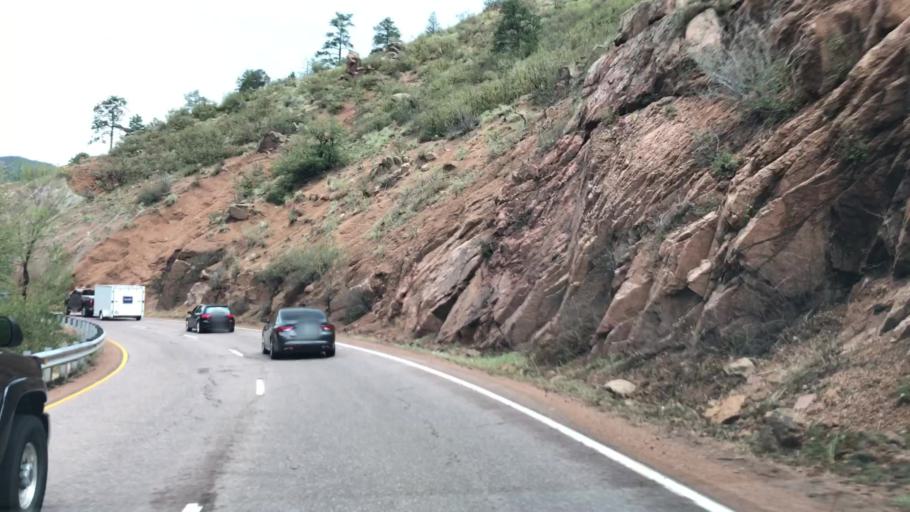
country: US
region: Colorado
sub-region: El Paso County
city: Manitou Springs
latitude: 38.8873
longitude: -104.9537
